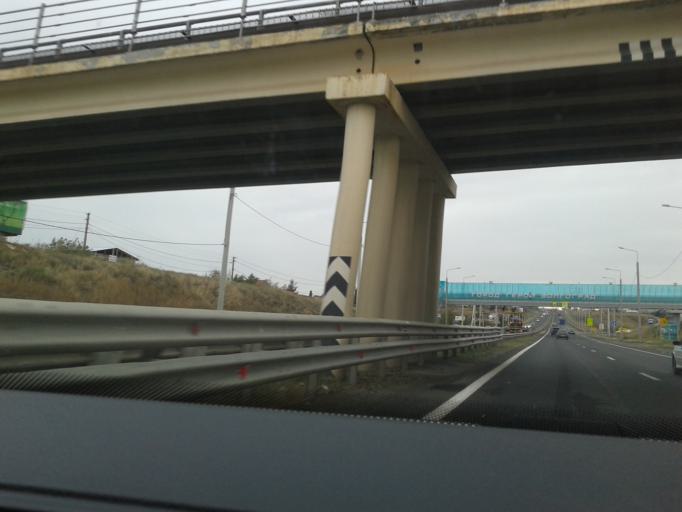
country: RU
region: Volgograd
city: Gorodishche
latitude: 48.7923
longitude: 44.4588
